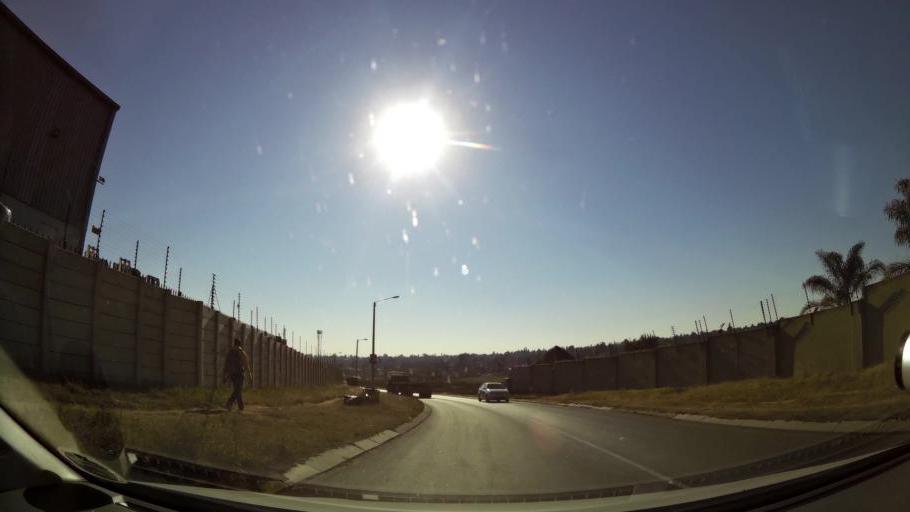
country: ZA
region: Gauteng
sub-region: City of Johannesburg Metropolitan Municipality
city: Modderfontein
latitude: -26.0666
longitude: 28.1951
